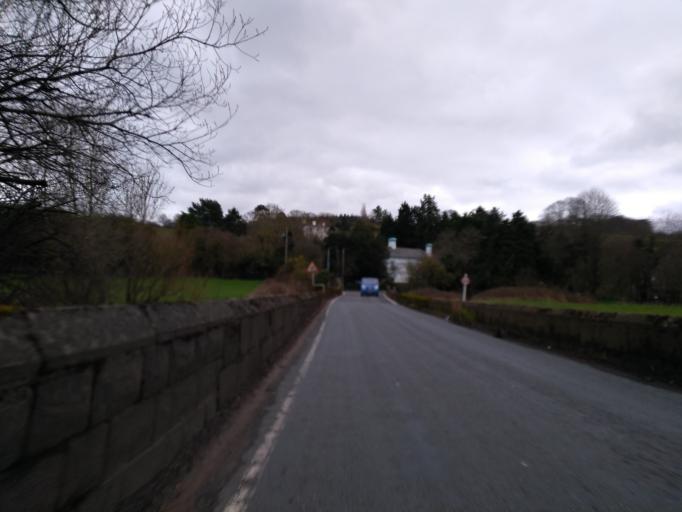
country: GB
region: England
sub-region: Devon
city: Heavitree
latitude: 50.7668
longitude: -3.5067
